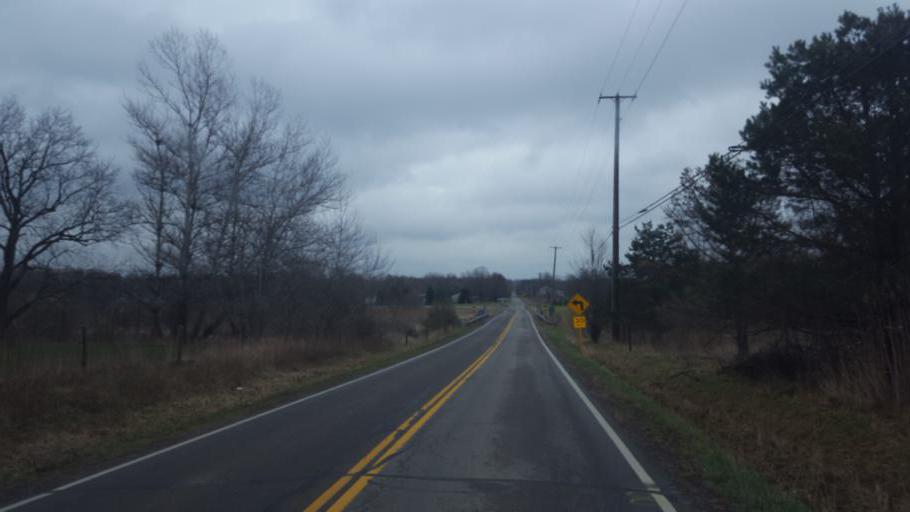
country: US
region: Ohio
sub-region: Medina County
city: Westfield Center
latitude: 41.0512
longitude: -81.9015
